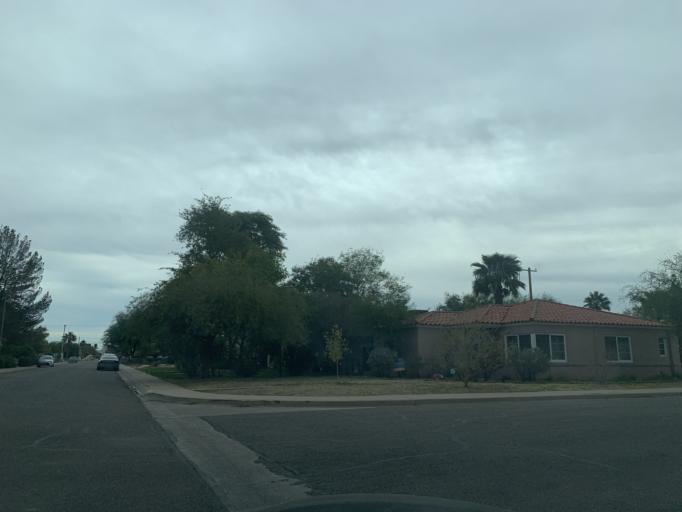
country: US
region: Arizona
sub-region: Maricopa County
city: Phoenix
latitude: 33.4685
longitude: -112.0499
